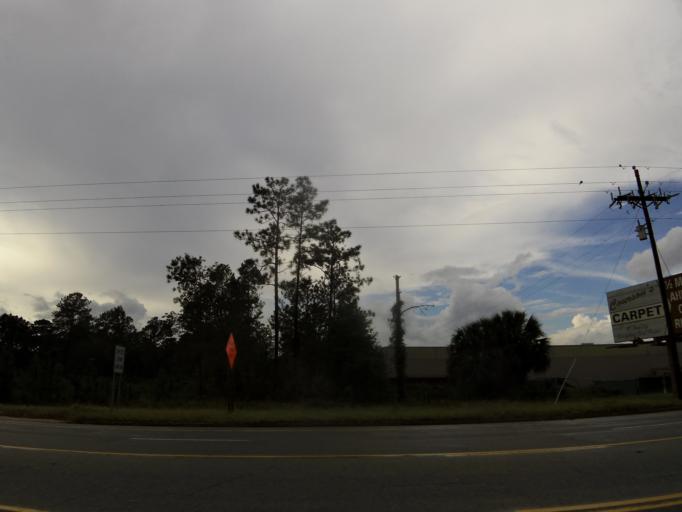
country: US
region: Georgia
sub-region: Wayne County
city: Jesup
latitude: 31.6282
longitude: -81.8658
